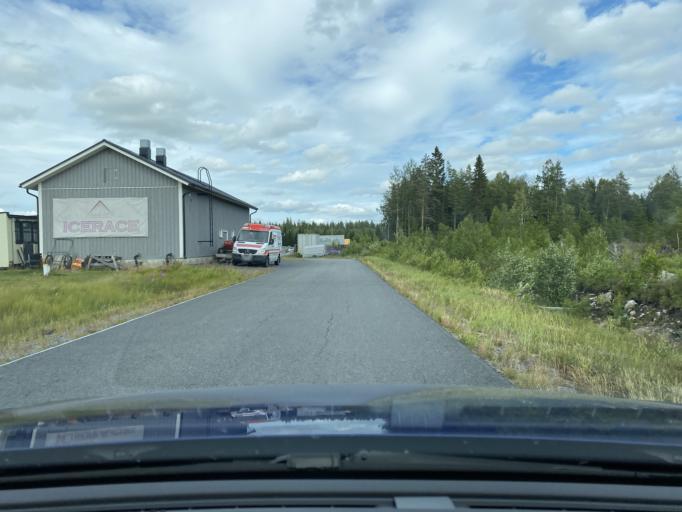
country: FI
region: Southern Ostrobothnia
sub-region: Seinaejoki
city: Jurva
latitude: 62.6225
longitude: 22.0327
